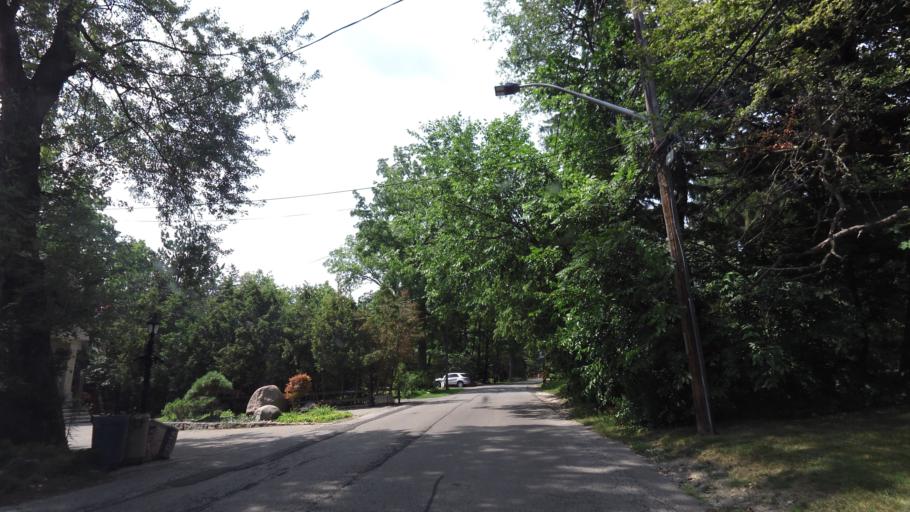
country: CA
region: Ontario
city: Mississauga
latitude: 43.5550
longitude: -79.5988
